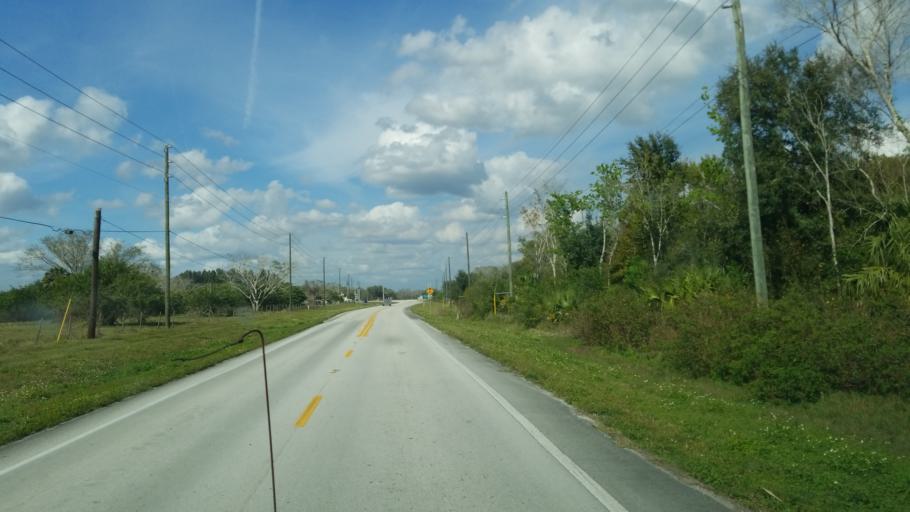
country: US
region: Florida
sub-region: Osceola County
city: Saint Cloud
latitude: 28.1403
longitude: -81.0763
